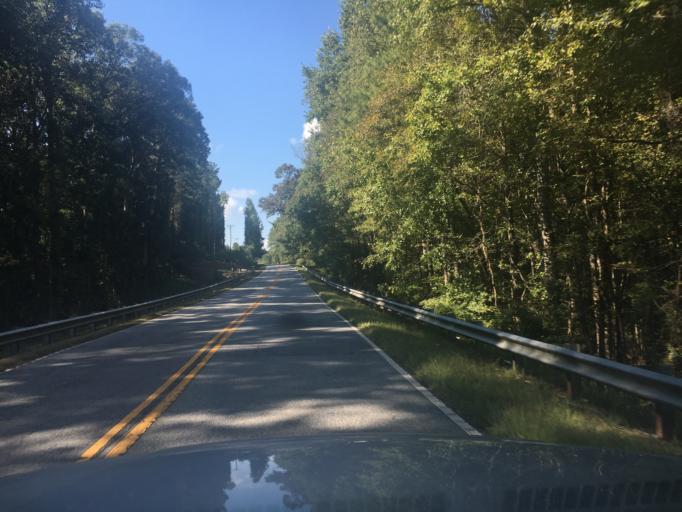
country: US
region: South Carolina
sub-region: Greenwood County
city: Greenwood
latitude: 34.2619
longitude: -82.1835
